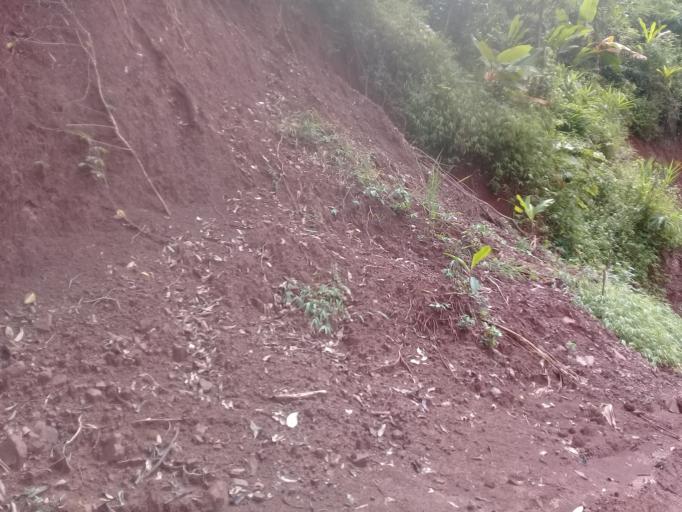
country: VN
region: Huyen Dien Bien
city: Thi Tran Muong Cha
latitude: 21.6752
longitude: 102.9141
